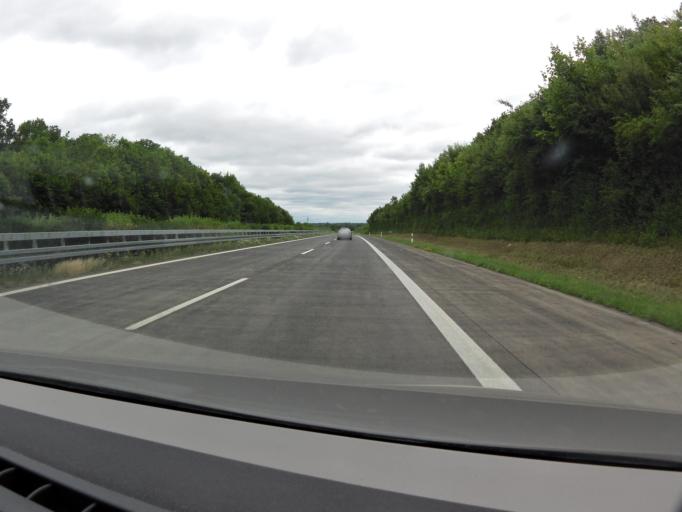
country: DE
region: Baden-Wuerttemberg
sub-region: Regierungsbezirk Stuttgart
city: Buch am Ahorn
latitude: 49.4910
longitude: 9.5649
